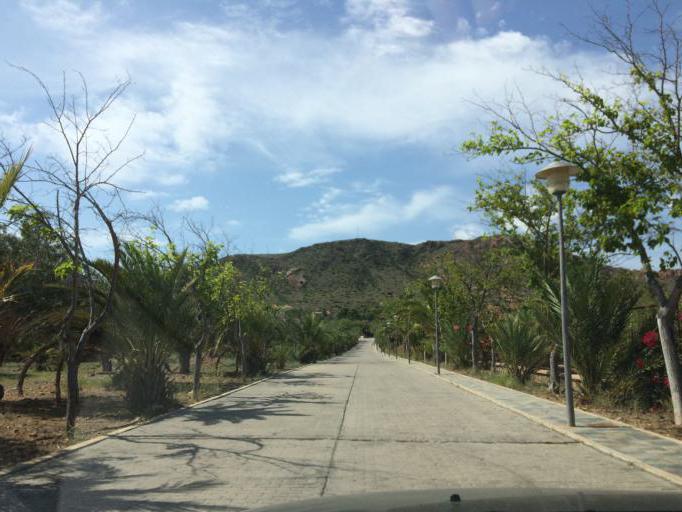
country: ES
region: Andalusia
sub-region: Provincia de Almeria
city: San Jose
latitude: 36.8486
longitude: -2.0403
